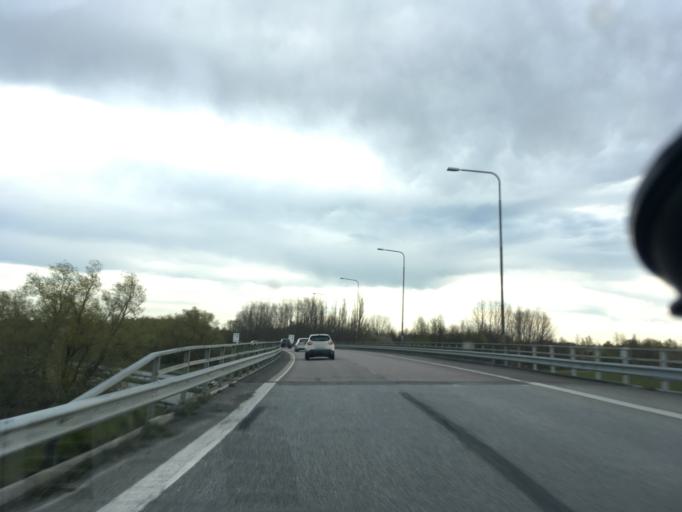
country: SE
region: Skane
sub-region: Vellinge Kommun
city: Vellinge
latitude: 55.4597
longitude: 13.0128
